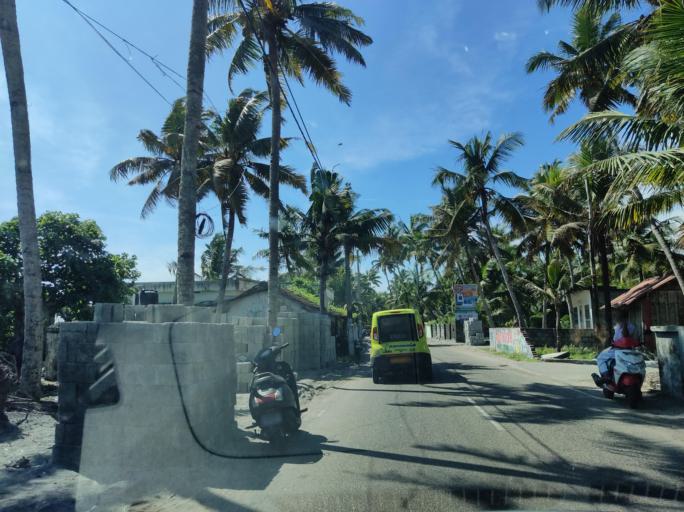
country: IN
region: Kerala
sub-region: Alappuzha
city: Kayankulam
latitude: 9.2230
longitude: 76.4240
